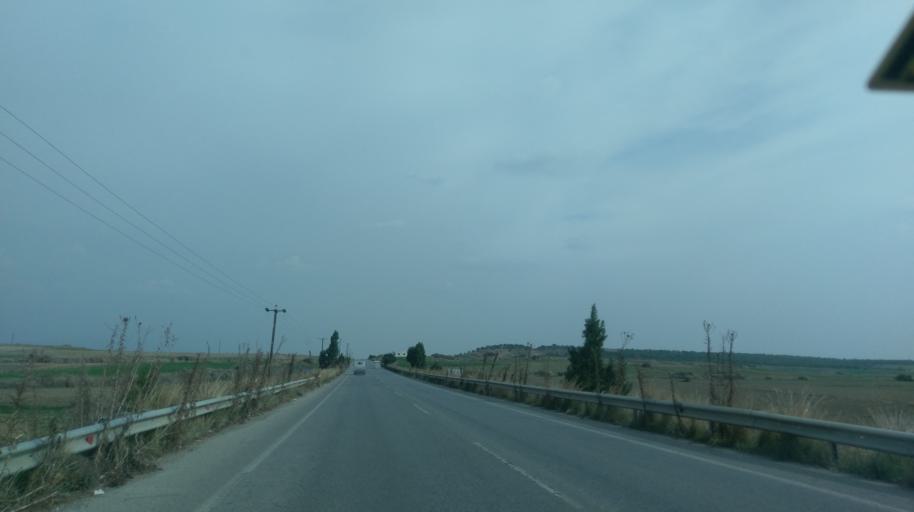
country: CY
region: Ammochostos
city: Lefkonoiko
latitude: 35.2347
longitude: 33.5708
